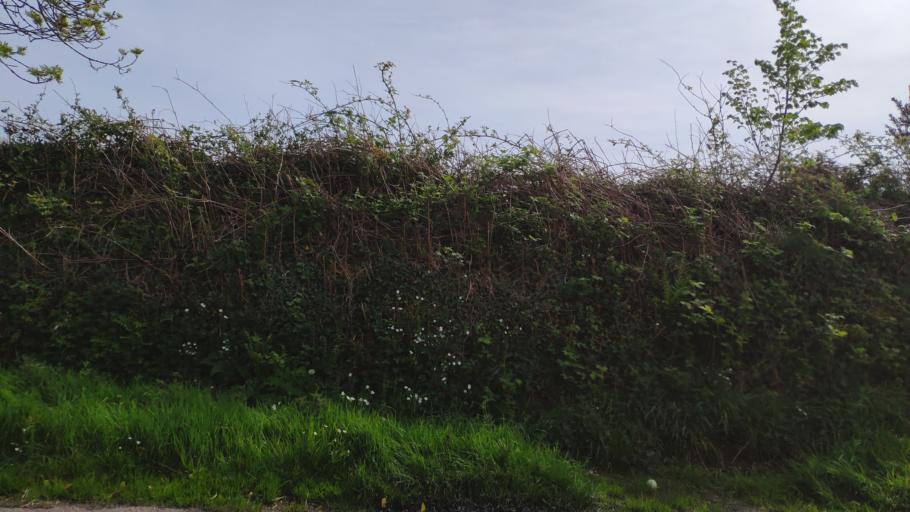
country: IE
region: Munster
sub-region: County Cork
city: Blarney
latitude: 51.9616
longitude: -8.5137
